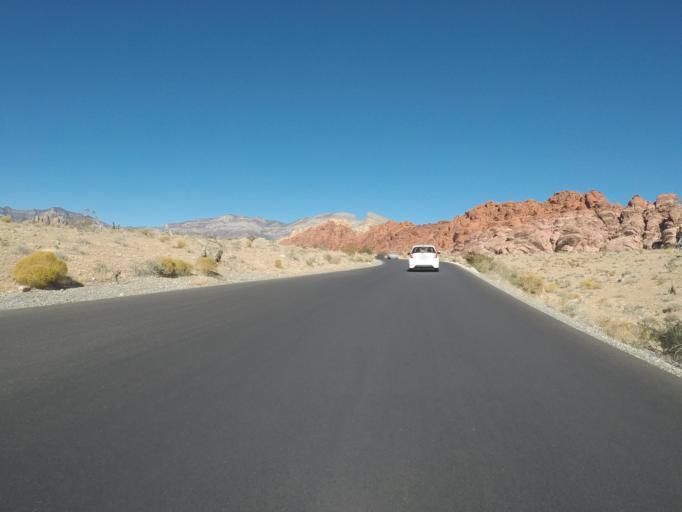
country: US
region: Nevada
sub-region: Clark County
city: Summerlin South
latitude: 36.1431
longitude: -115.4287
